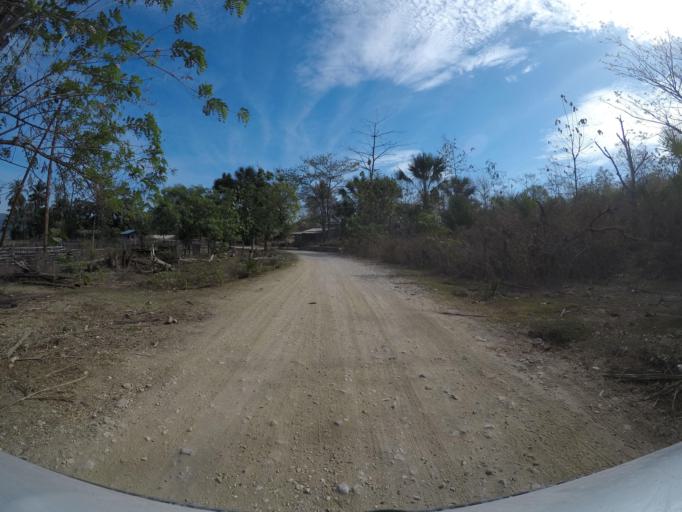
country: TL
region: Bobonaro
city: Maliana
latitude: -8.8846
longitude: 125.2089
